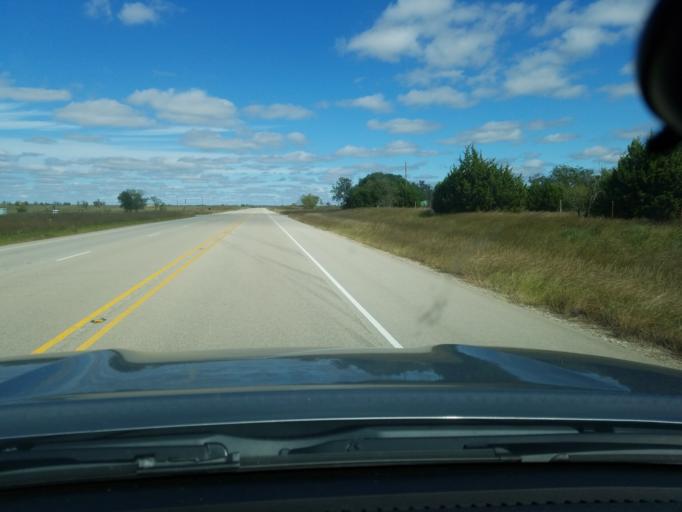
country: US
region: Texas
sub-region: Hamilton County
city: Hamilton
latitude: 31.6251
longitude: -98.1551
